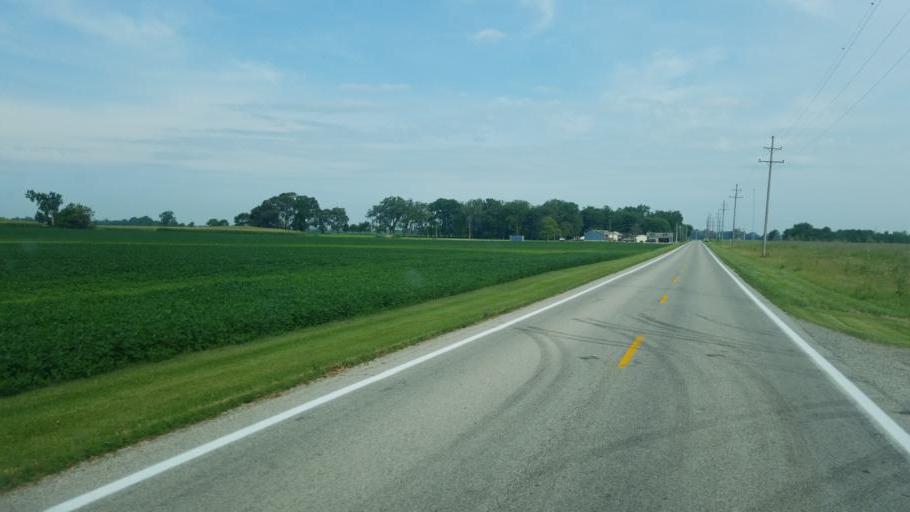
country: US
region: Ohio
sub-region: Marion County
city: Marion
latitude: 40.5522
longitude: -83.1950
